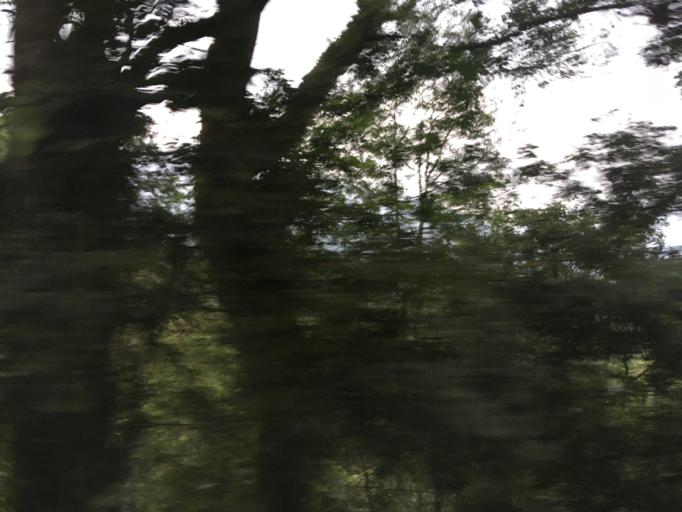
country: TW
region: Taiwan
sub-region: Chiayi
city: Jiayi Shi
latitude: 23.5386
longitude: 120.6250
